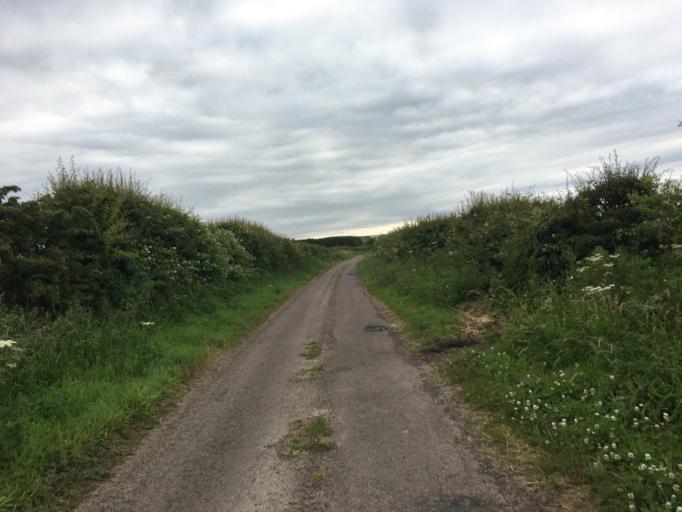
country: GB
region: England
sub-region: Northumberland
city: Lowick
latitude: 55.6576
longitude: -1.9046
